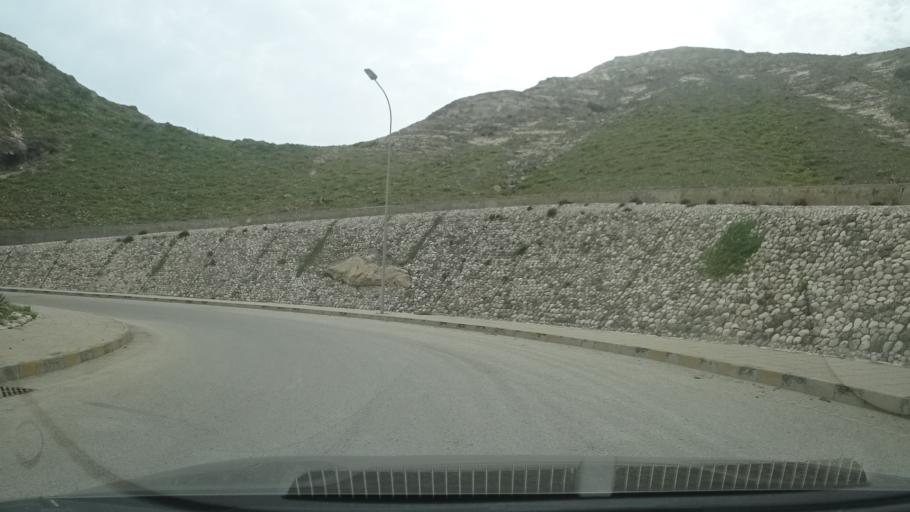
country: OM
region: Zufar
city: Salalah
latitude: 16.8774
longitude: 53.7674
